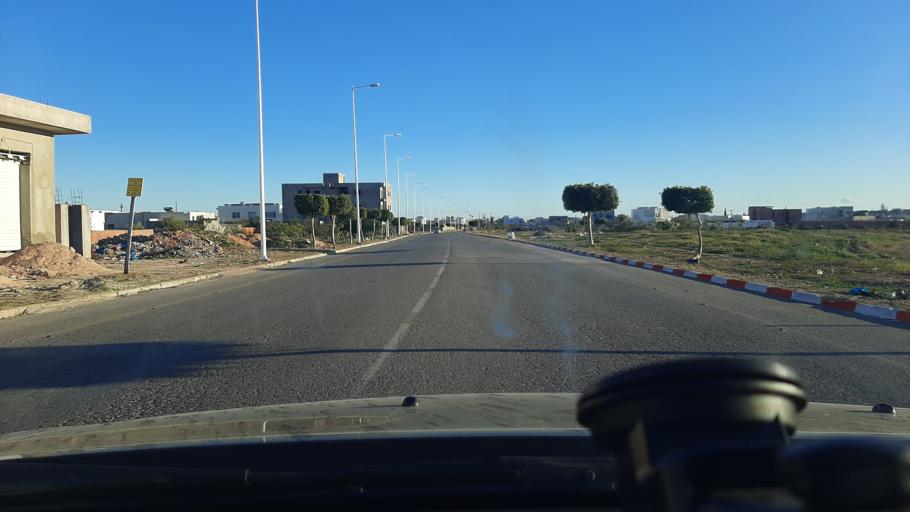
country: TN
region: Safaqis
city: Sfax
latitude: 34.8052
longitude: 10.7144
